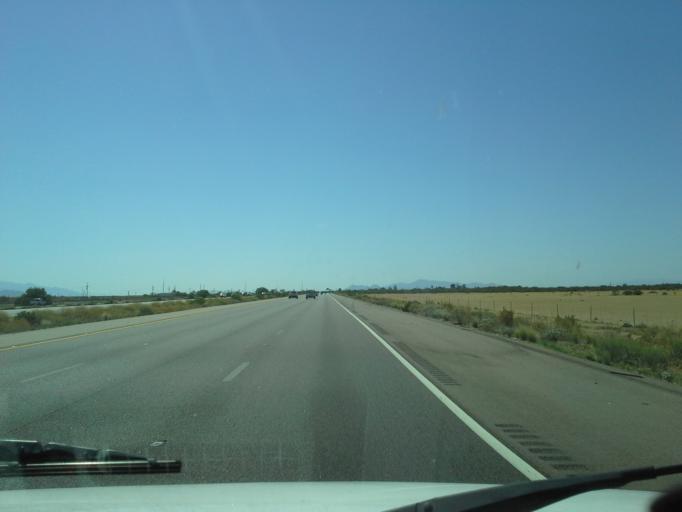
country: US
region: Arizona
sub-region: Pima County
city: Avra Valley
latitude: 32.5963
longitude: -111.3425
